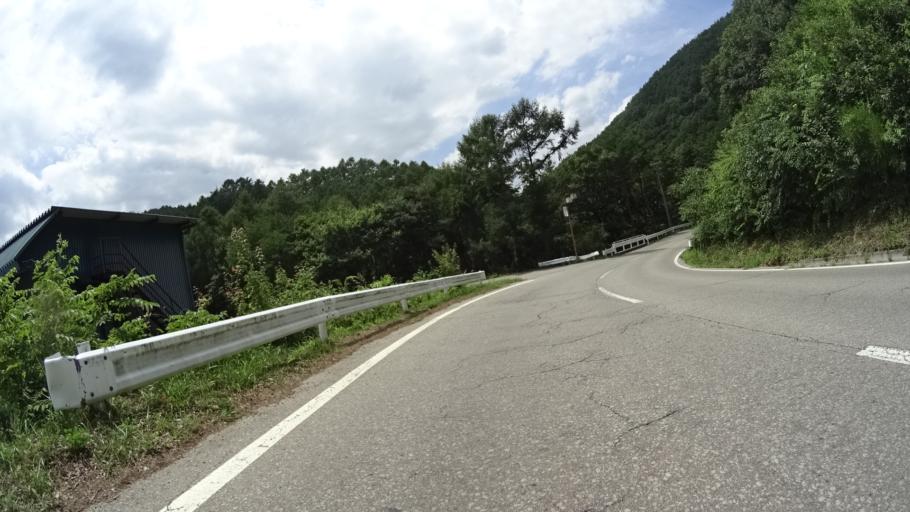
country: JP
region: Nagano
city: Saku
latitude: 36.0600
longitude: 138.5714
